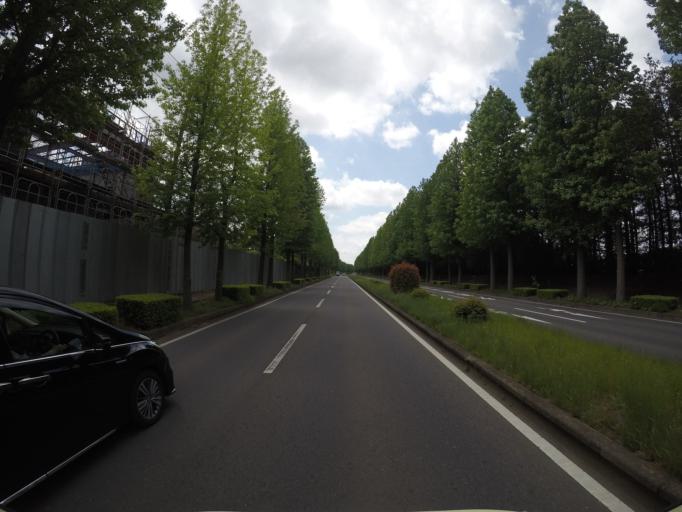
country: JP
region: Ibaraki
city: Naka
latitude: 36.0499
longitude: 140.1017
